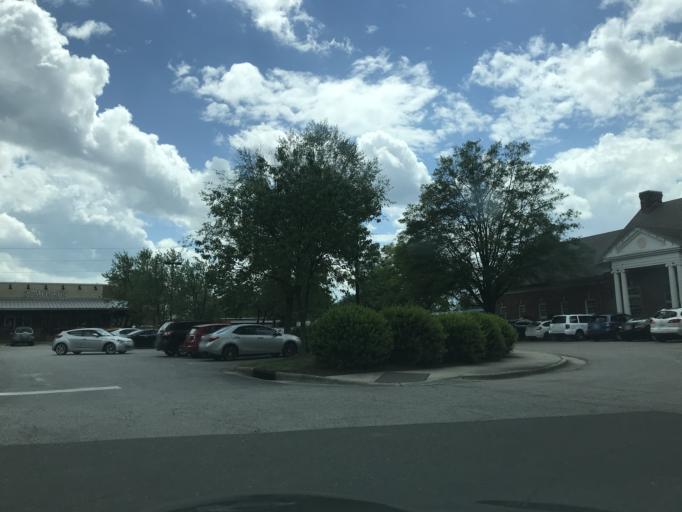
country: US
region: North Carolina
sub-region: Wake County
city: Raleigh
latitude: 35.7901
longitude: -78.6401
